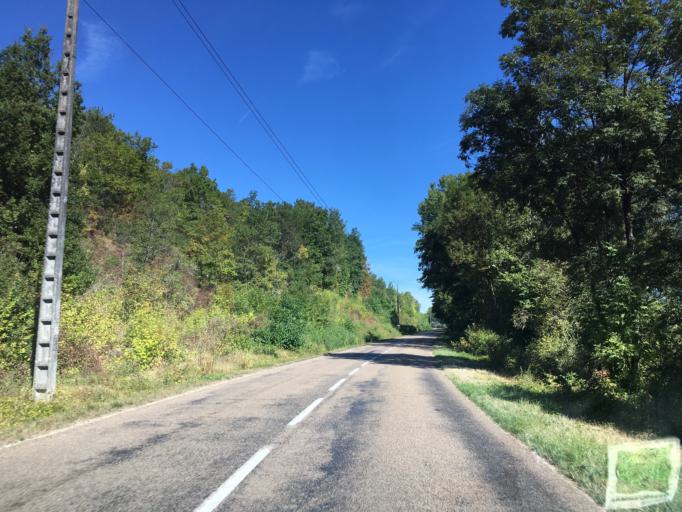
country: FR
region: Bourgogne
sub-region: Departement de l'Yonne
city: Vermenton
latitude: 47.6360
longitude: 3.6567
